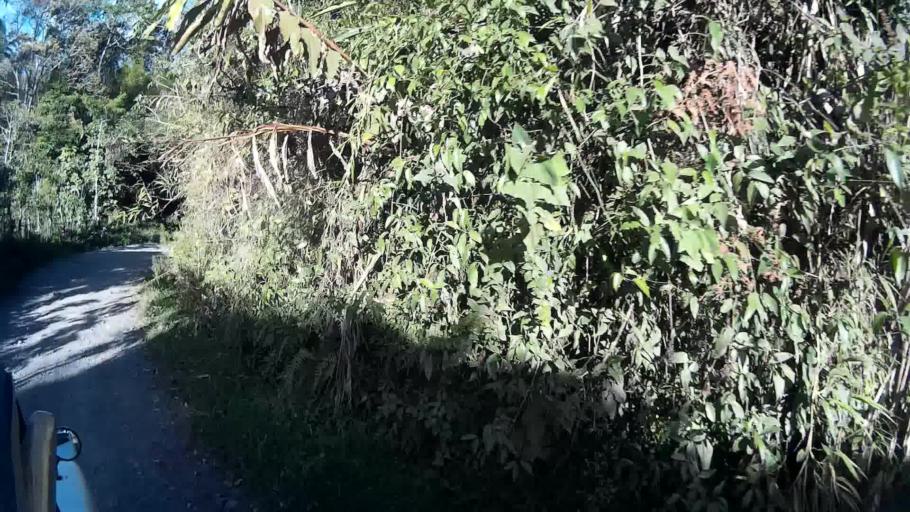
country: CO
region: Quindio
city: Filandia
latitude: 4.7130
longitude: -75.6630
